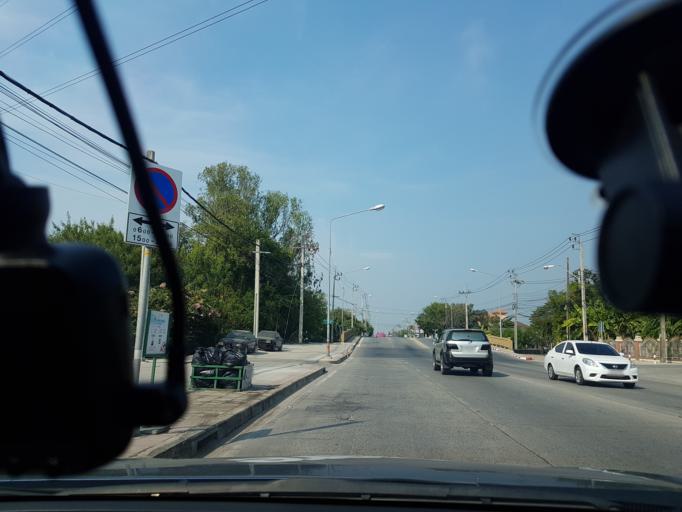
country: TH
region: Bangkok
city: Khlong Sam Wa
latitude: 13.8788
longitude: 100.7223
